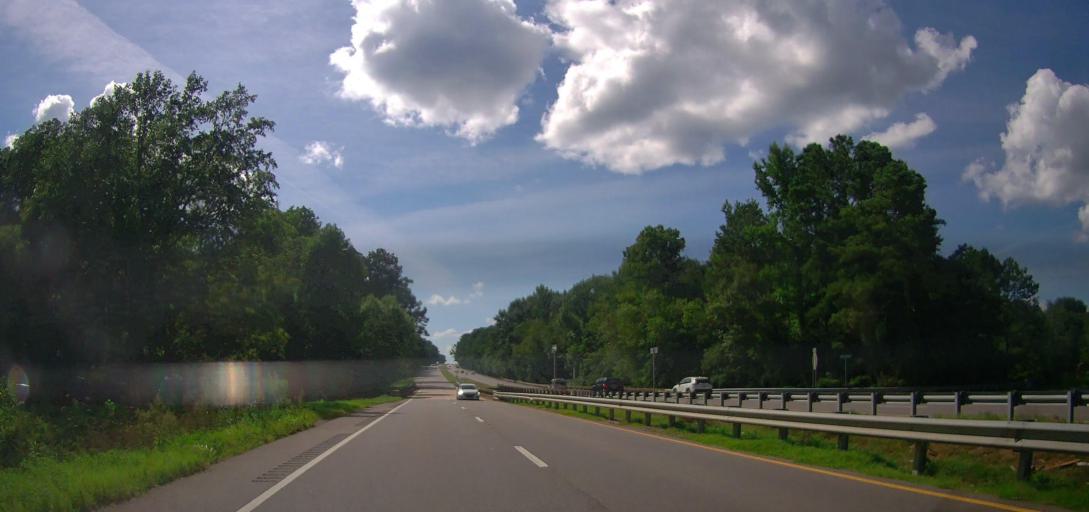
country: US
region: Alabama
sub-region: Tuscaloosa County
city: Northport
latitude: 33.2468
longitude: -87.6758
